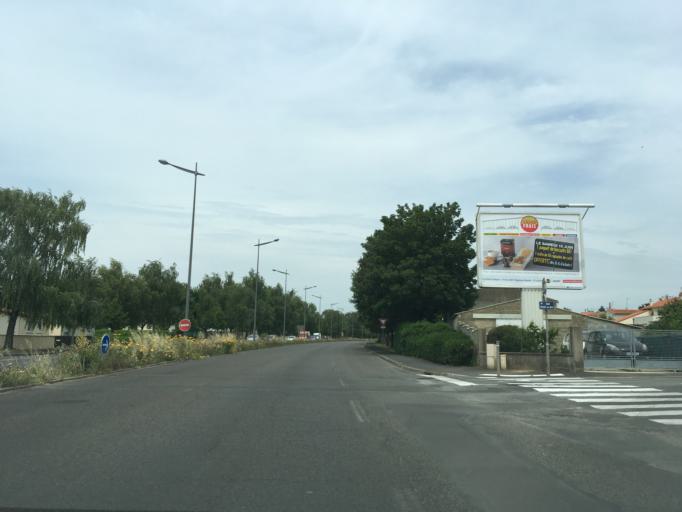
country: FR
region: Poitou-Charentes
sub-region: Departement des Deux-Sevres
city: Niort
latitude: 46.3206
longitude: -0.4862
